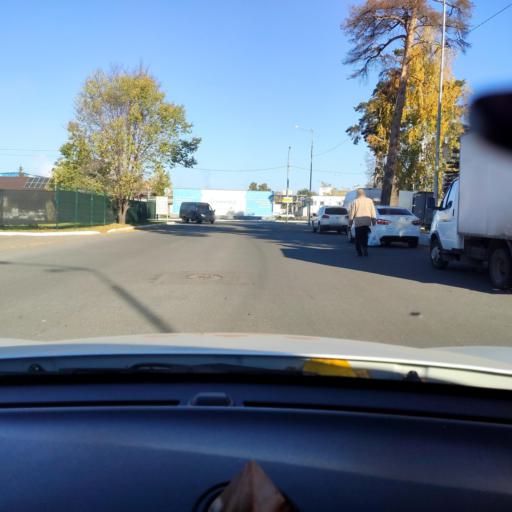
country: RU
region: Tatarstan
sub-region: Gorod Kazan'
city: Kazan
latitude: 55.8341
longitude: 49.0508
